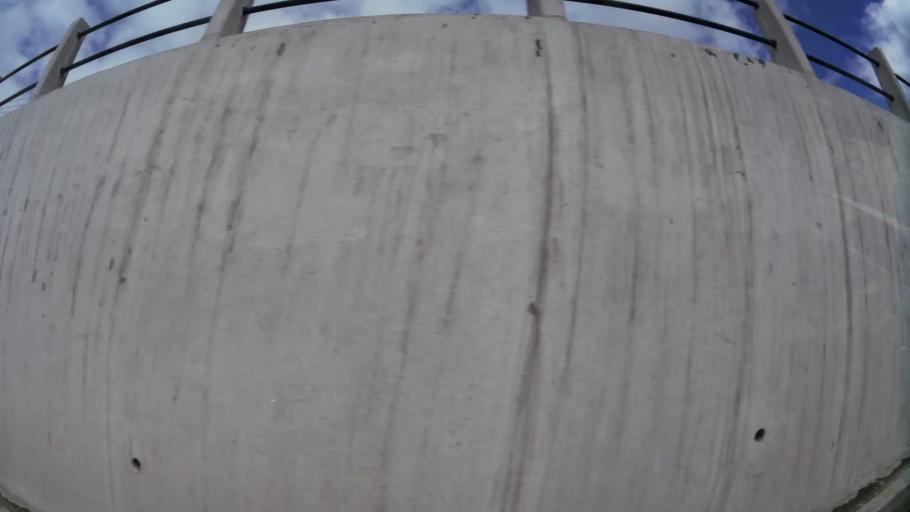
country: GT
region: Guatemala
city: Mixco
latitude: 14.6168
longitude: -90.6060
